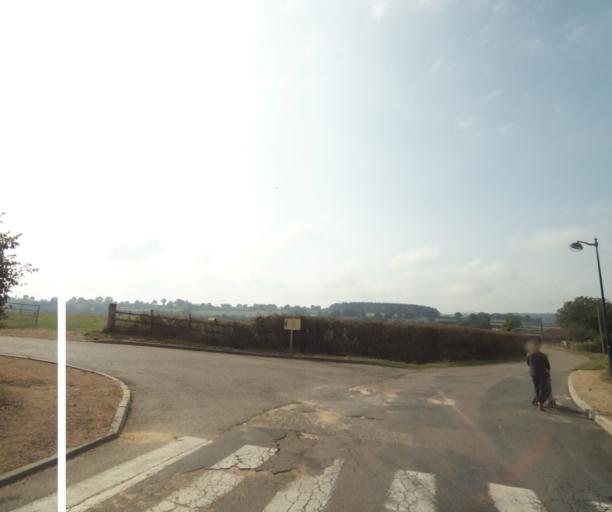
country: FR
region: Bourgogne
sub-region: Departement de Saone-et-Loire
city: Charolles
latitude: 46.4289
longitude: 4.2693
